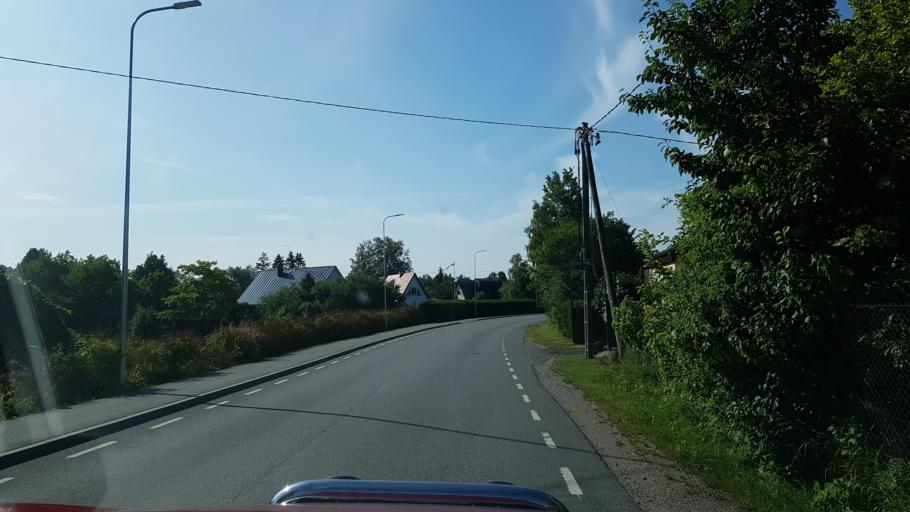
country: EE
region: Harju
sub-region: Joelaehtme vald
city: Loo
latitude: 59.3900
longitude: 24.9350
